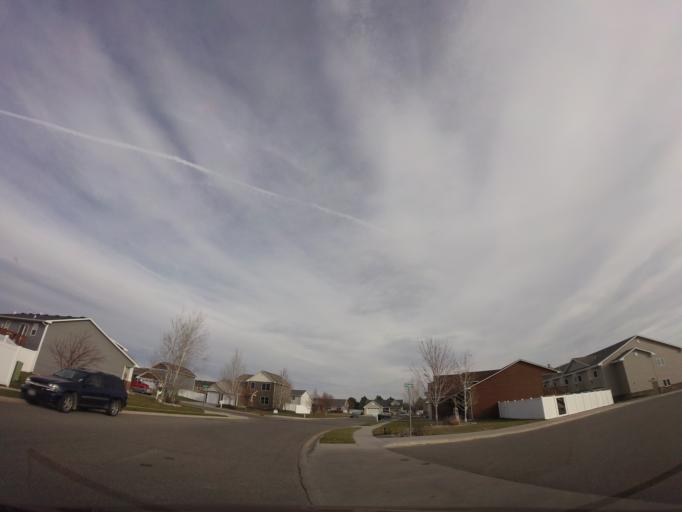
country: US
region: Montana
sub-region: Yellowstone County
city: Billings
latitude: 45.7858
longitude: -108.6104
